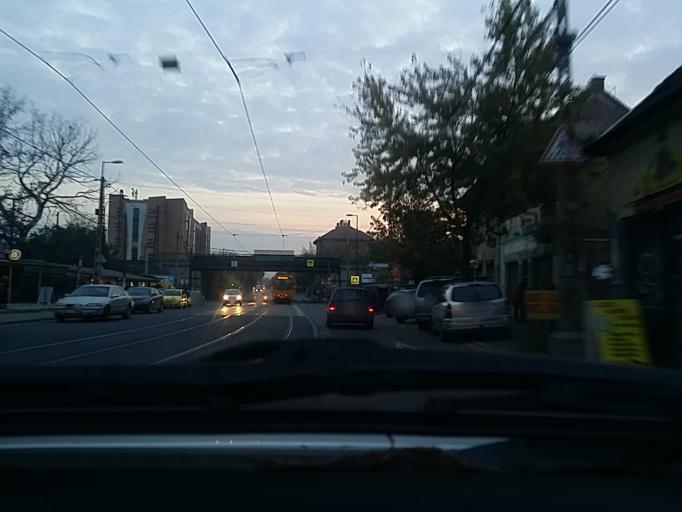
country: HU
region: Budapest
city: Budapest XIV. keruelet
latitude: 47.5366
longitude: 19.1145
